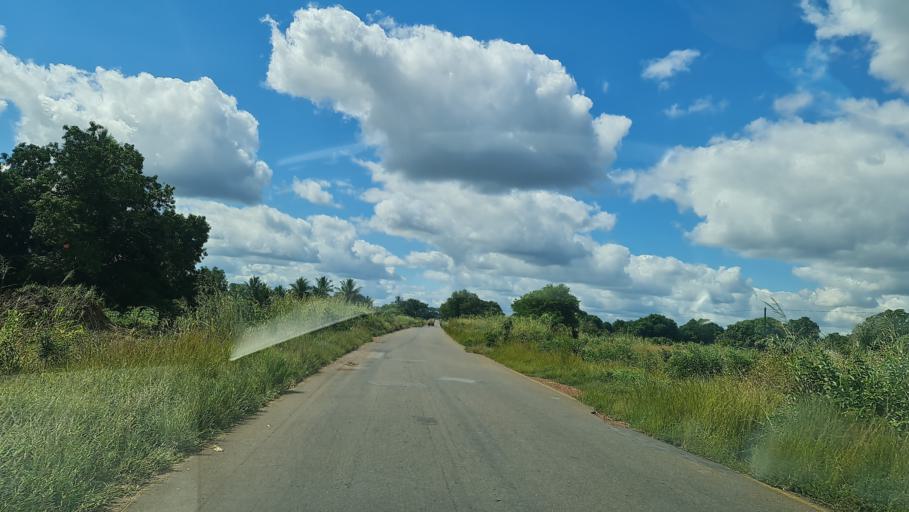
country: MZ
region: Zambezia
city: Quelimane
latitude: -17.5163
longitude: 36.2200
